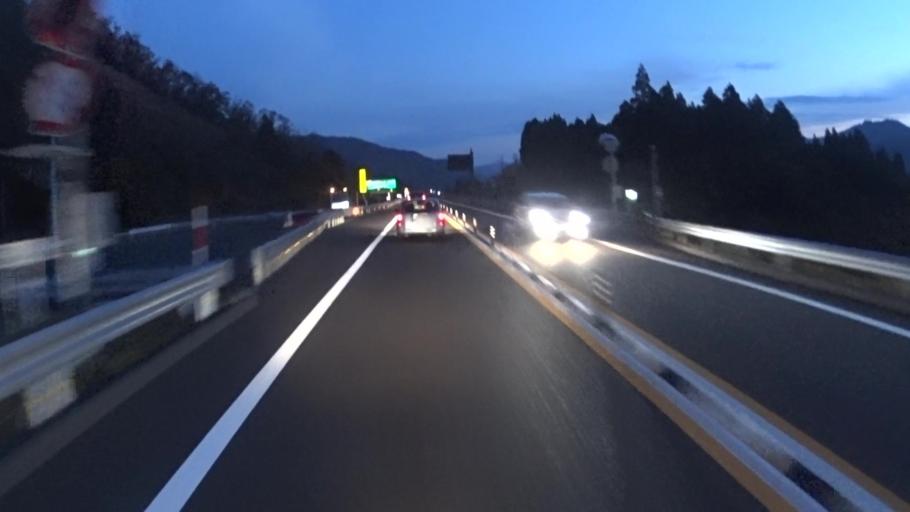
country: JP
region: Kyoto
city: Ayabe
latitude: 35.3011
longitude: 135.3309
